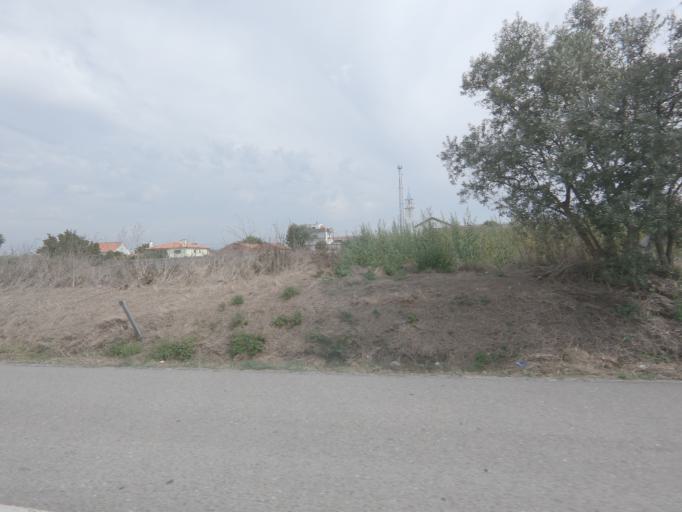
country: PT
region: Leiria
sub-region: Pombal
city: Pombal
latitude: 39.8748
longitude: -8.6866
